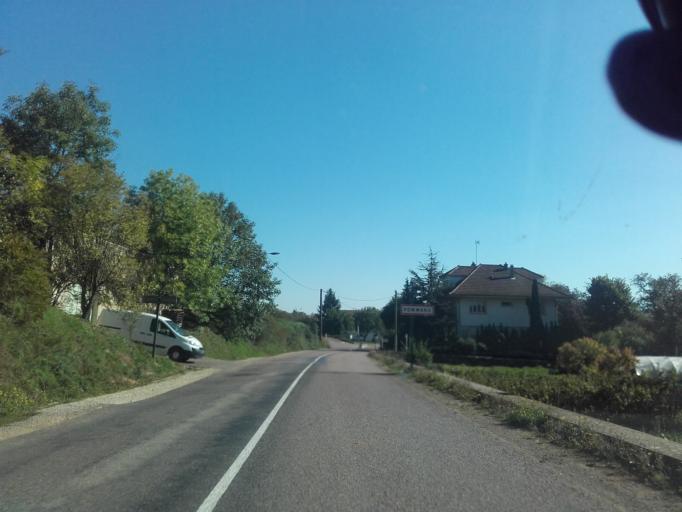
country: FR
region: Bourgogne
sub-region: Departement de la Cote-d'Or
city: Meursault
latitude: 47.0144
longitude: 4.7910
